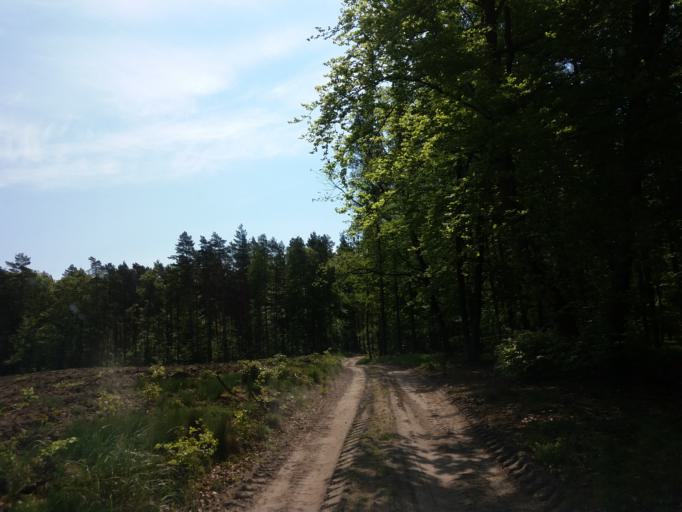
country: PL
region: West Pomeranian Voivodeship
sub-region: Powiat choszczenski
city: Bierzwnik
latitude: 53.0883
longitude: 15.7591
